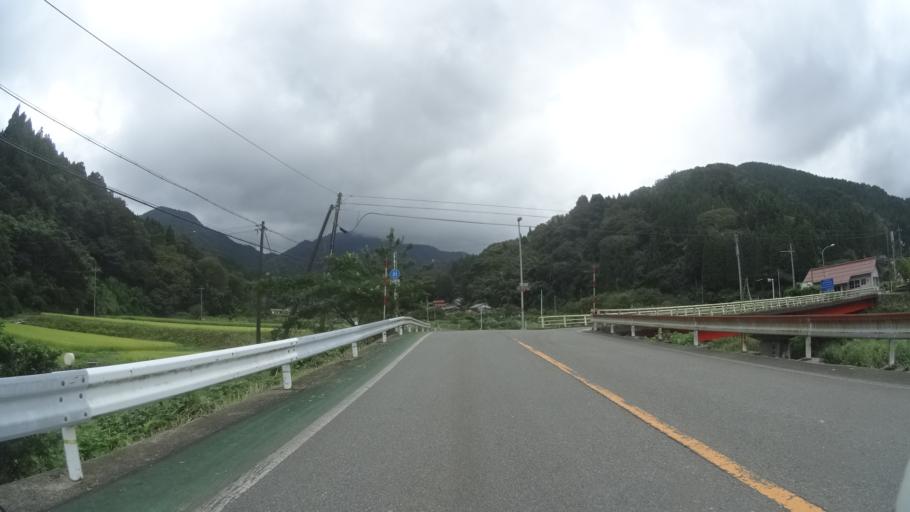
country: JP
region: Tottori
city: Kurayoshi
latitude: 35.4155
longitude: 134.0198
